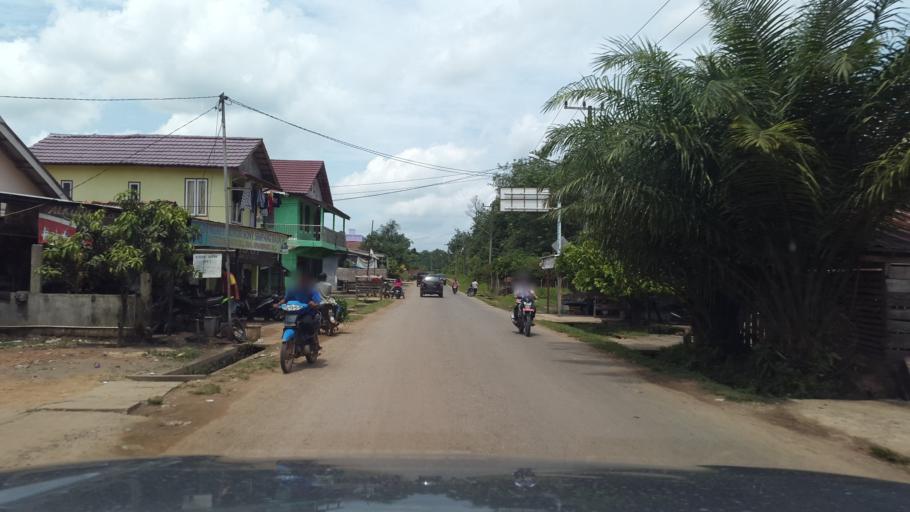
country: ID
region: South Sumatra
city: Gunungmegang Dalam
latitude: -3.3180
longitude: 103.8985
